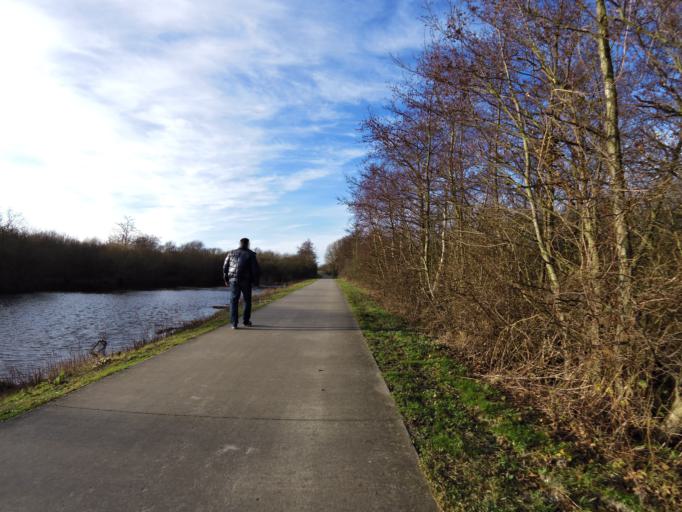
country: NL
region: South Holland
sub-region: Gemeente Rotterdam
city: Hoek van Holland
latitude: 51.9144
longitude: 4.0693
